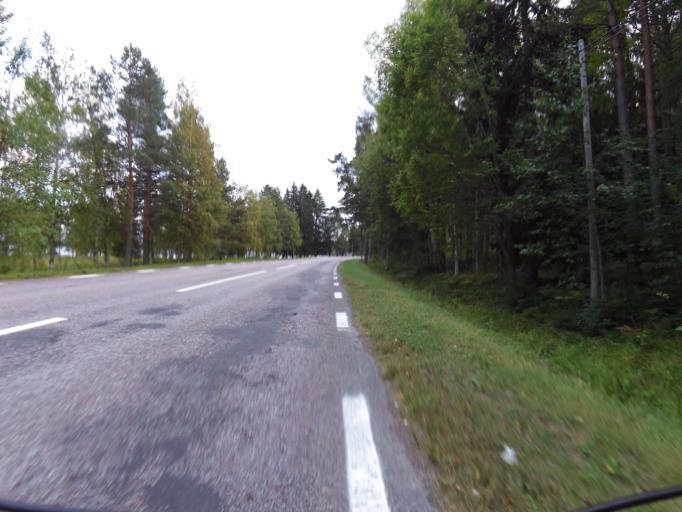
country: SE
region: Gaevleborg
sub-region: Sandvikens Kommun
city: Sandviken
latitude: 60.7068
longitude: 16.8115
